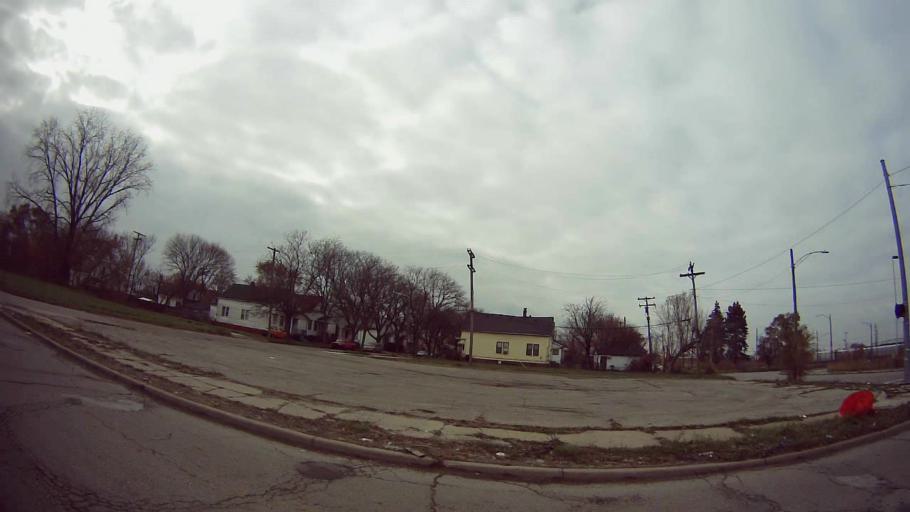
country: US
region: Michigan
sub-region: Wayne County
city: Hamtramck
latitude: 42.4014
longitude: -83.0378
